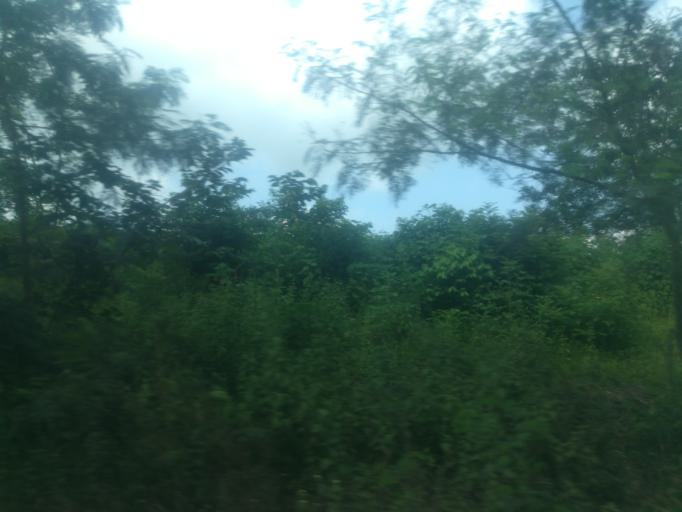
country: NG
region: Oyo
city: Moniya
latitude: 7.5841
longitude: 3.9151
